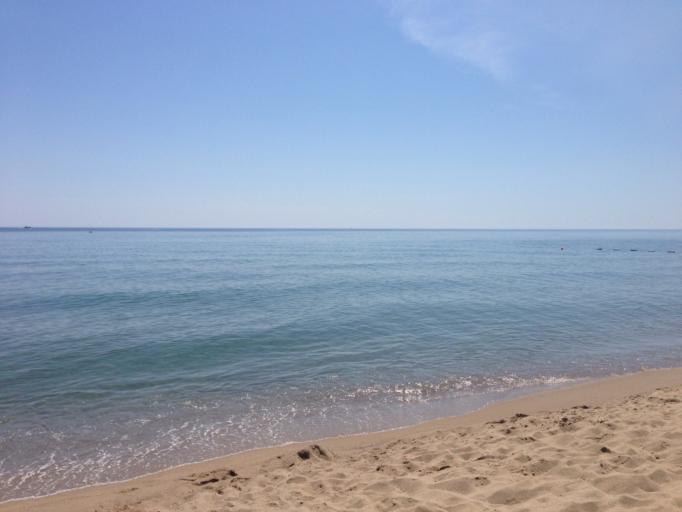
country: BG
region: Burgas
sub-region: Obshtina Nesebur
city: Obzor
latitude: 42.8306
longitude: 27.8827
